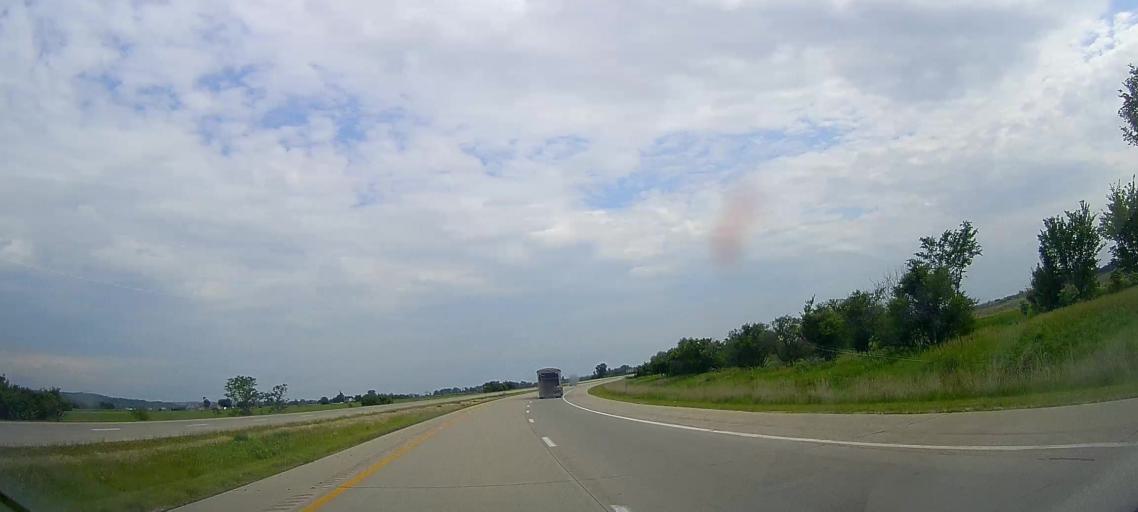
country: US
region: Nebraska
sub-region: Burt County
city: Tekamah
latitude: 41.7963
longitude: -96.0512
